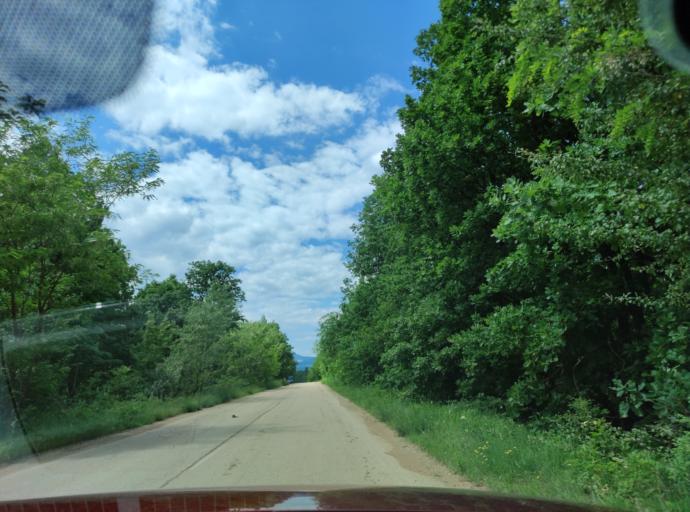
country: BG
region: Montana
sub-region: Obshtina Berkovitsa
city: Berkovitsa
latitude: 43.3677
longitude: 23.0842
